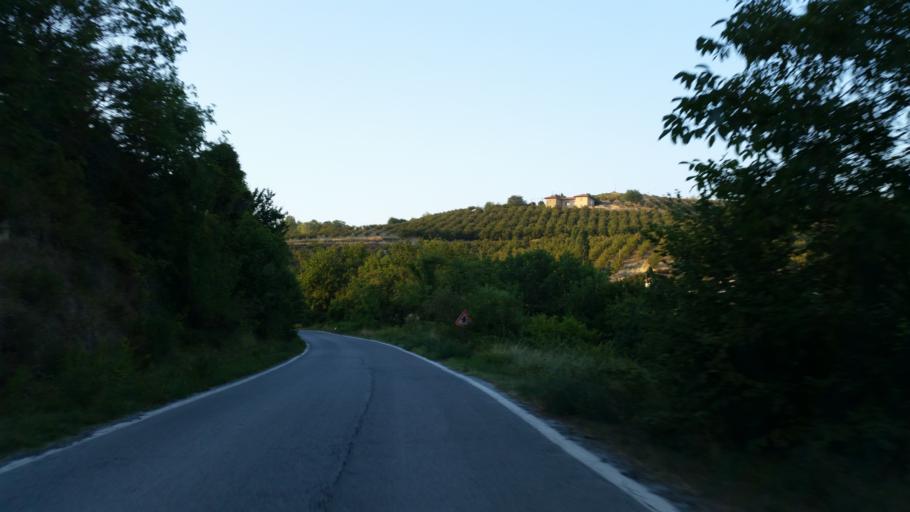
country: IT
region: Piedmont
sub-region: Provincia di Cuneo
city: Borgomale
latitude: 44.6539
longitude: 8.1344
